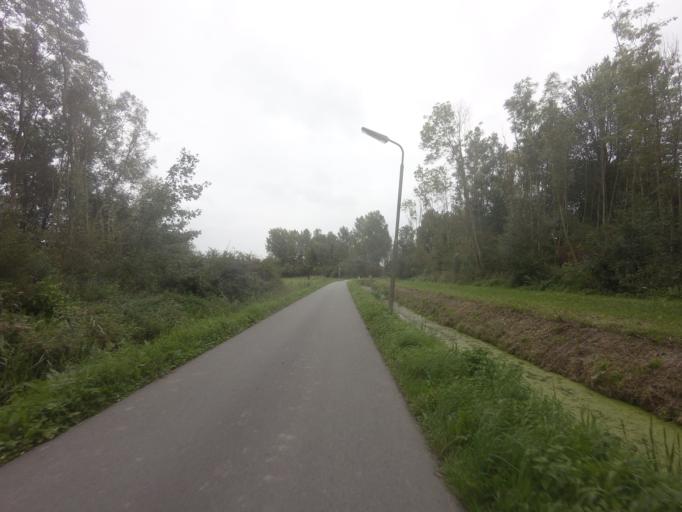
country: NL
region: Friesland
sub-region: Gemeente Leeuwarden
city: Bilgaard
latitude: 53.2214
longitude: 5.7898
